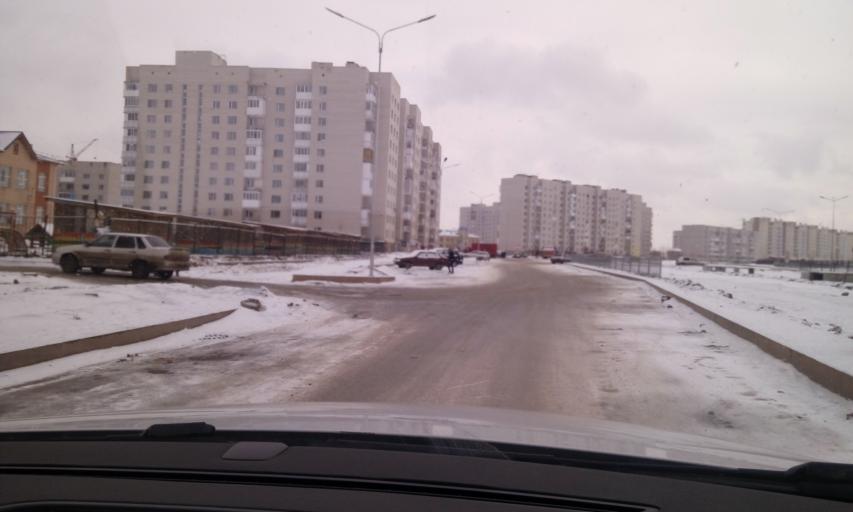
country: KZ
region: Astana Qalasy
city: Astana
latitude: 51.1272
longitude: 71.5040
